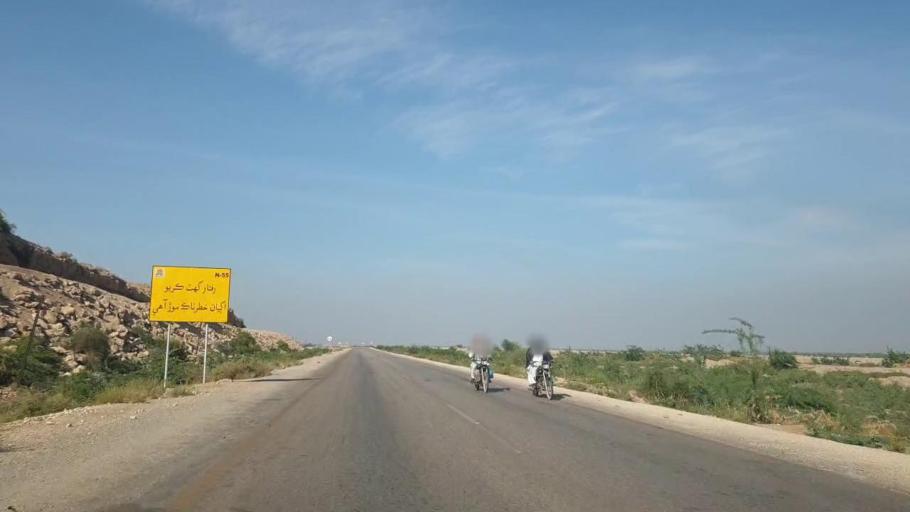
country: PK
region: Sindh
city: Sehwan
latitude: 26.3676
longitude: 67.8738
